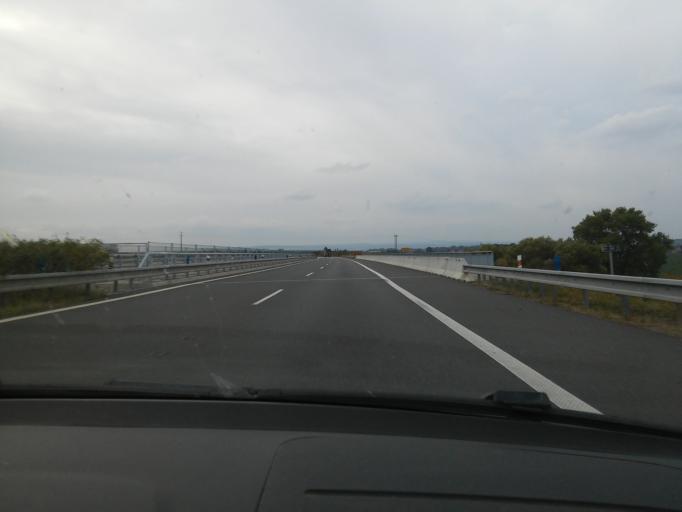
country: CZ
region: Olomoucky
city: Nemcice nad Hanou
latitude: 49.3242
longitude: 17.2408
